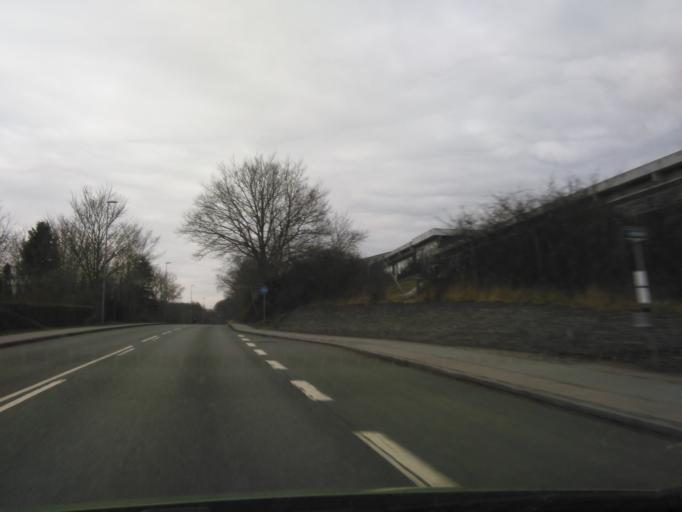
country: DK
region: North Denmark
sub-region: Mariagerfjord Kommune
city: Mariager
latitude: 56.6502
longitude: 9.9760
